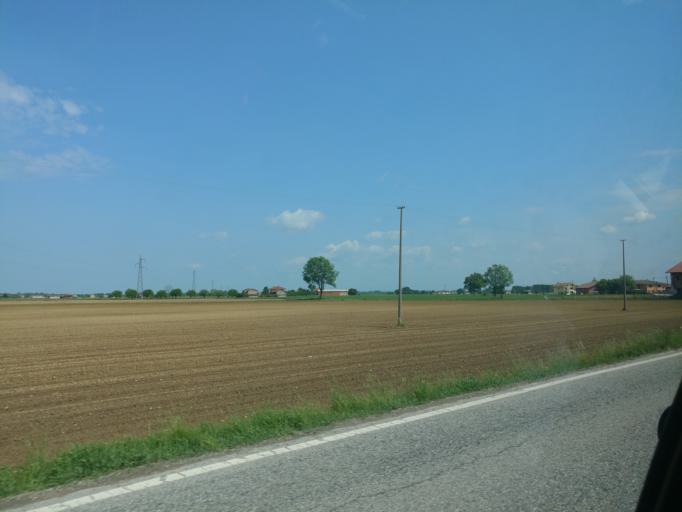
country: IT
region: Piedmont
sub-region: Provincia di Torino
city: Cavour
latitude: 44.7557
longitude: 7.4028
